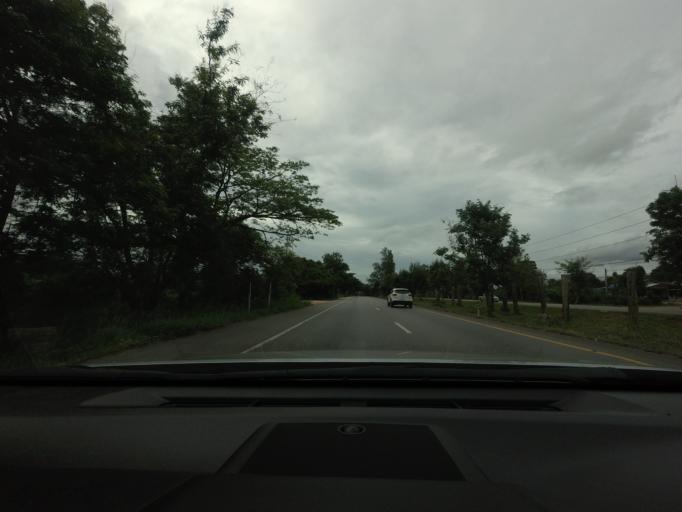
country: TH
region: Prachuap Khiri Khan
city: Hua Hin
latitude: 12.6179
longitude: 99.8593
